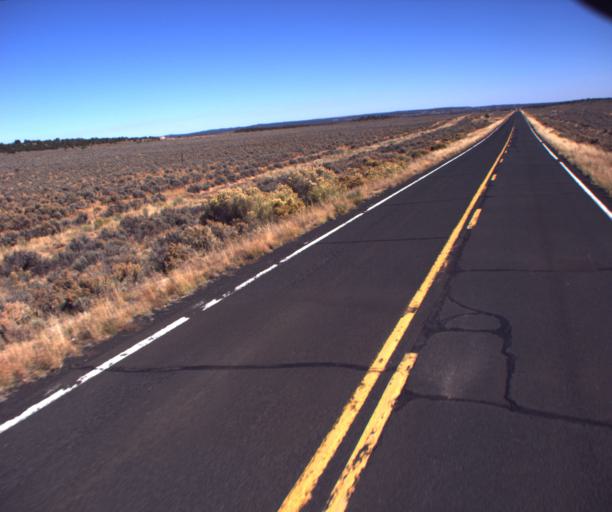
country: US
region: Arizona
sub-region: Navajo County
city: First Mesa
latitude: 35.7541
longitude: -110.0298
